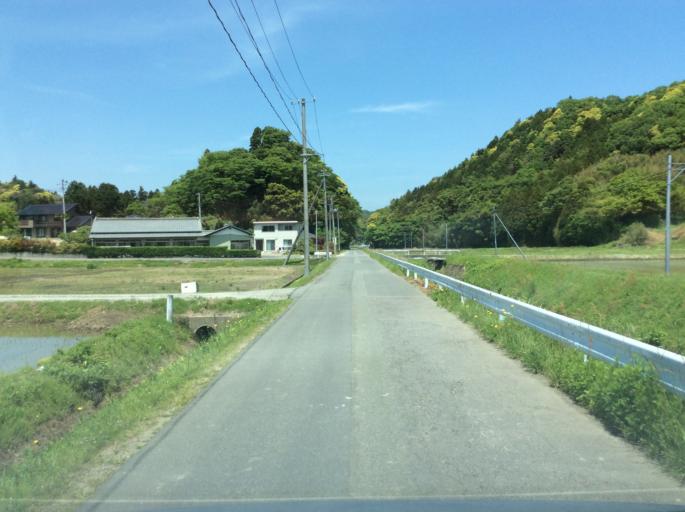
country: JP
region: Fukushima
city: Iwaki
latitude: 37.0199
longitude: 140.9388
